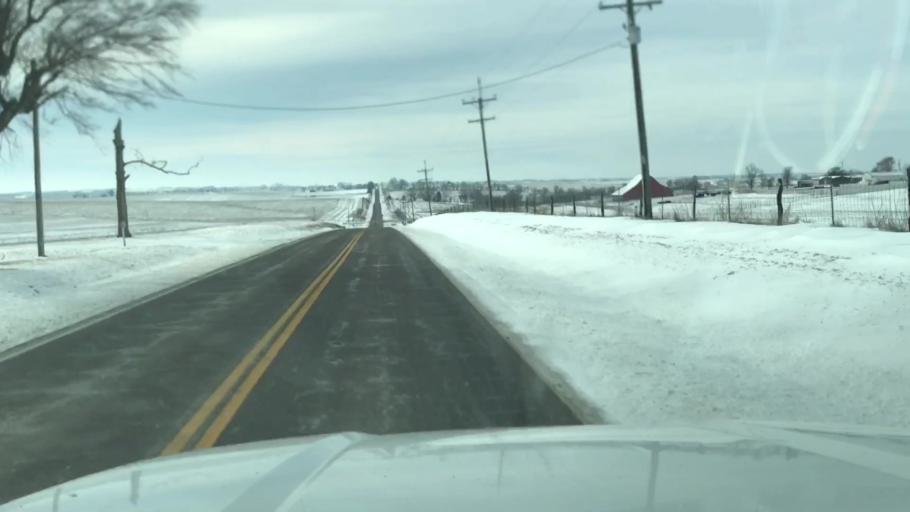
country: US
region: Missouri
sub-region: Holt County
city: Oregon
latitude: 40.0834
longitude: -95.1355
